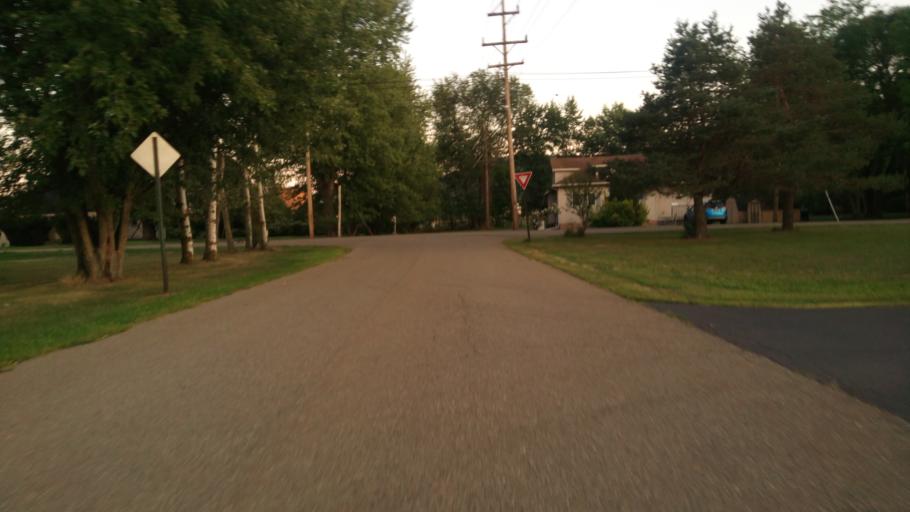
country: US
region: New York
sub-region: Chemung County
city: Southport
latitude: 42.0643
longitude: -76.7901
